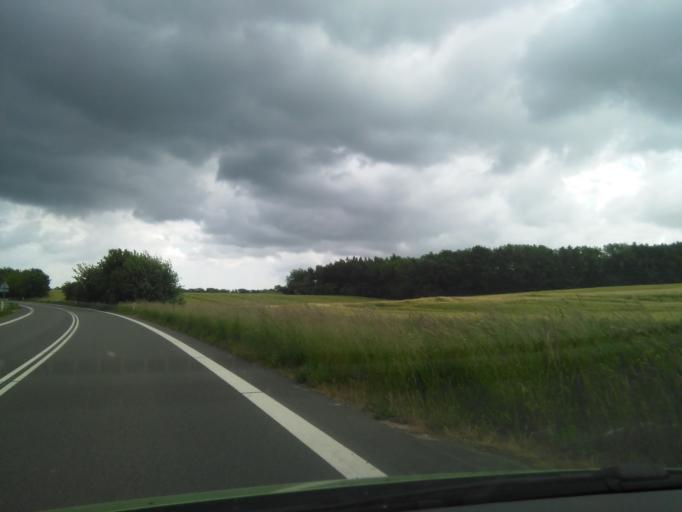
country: DK
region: Capital Region
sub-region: Bornholm Kommune
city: Akirkeby
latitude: 55.2213
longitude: 14.8967
